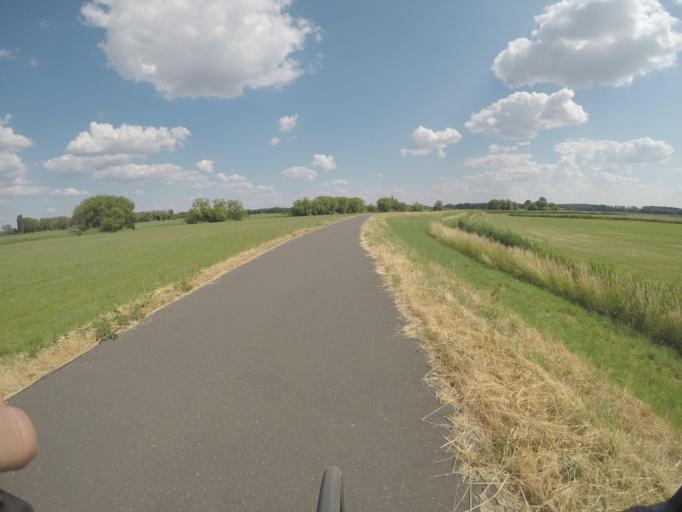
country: DE
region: Brandenburg
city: Ketzin
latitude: 52.4523
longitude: 12.8736
